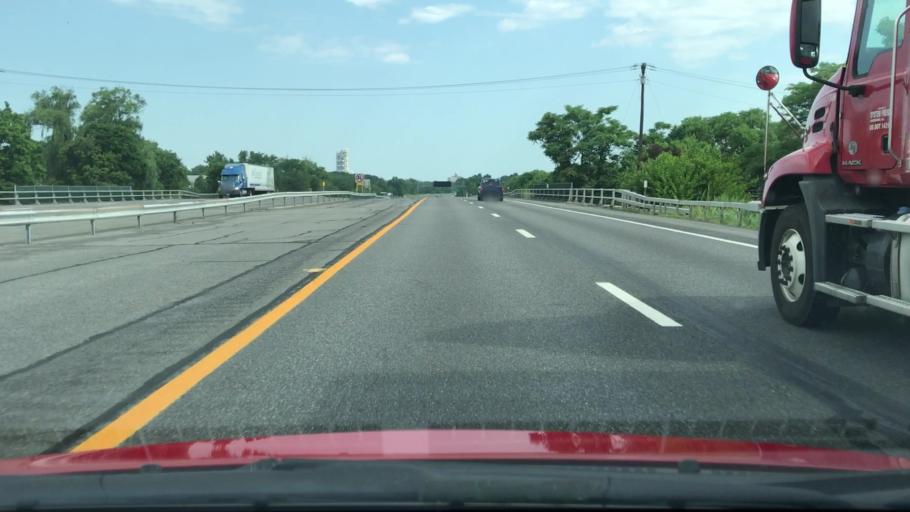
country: US
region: New York
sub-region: Albany County
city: Ravena
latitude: 42.4719
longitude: -73.8057
